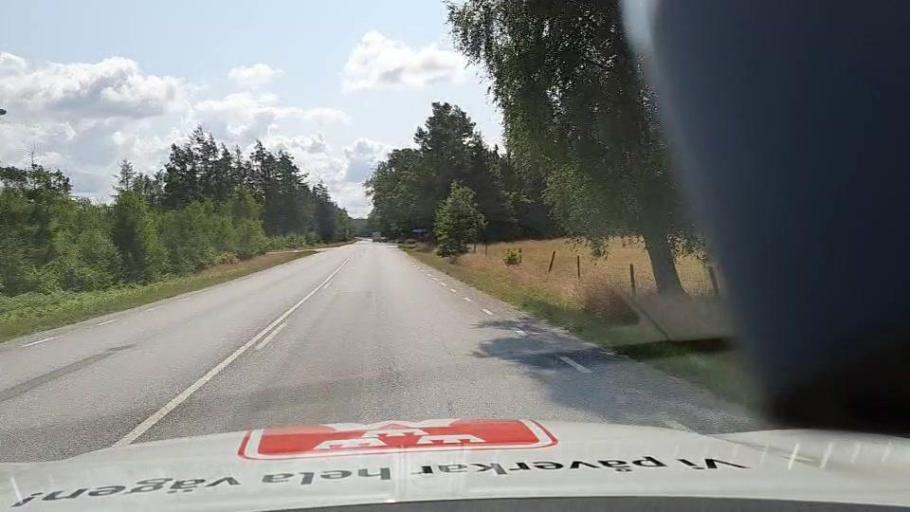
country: SE
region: Vaestra Goetaland
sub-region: Uddevalla Kommun
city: Ljungskile
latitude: 58.1318
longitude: 11.9802
